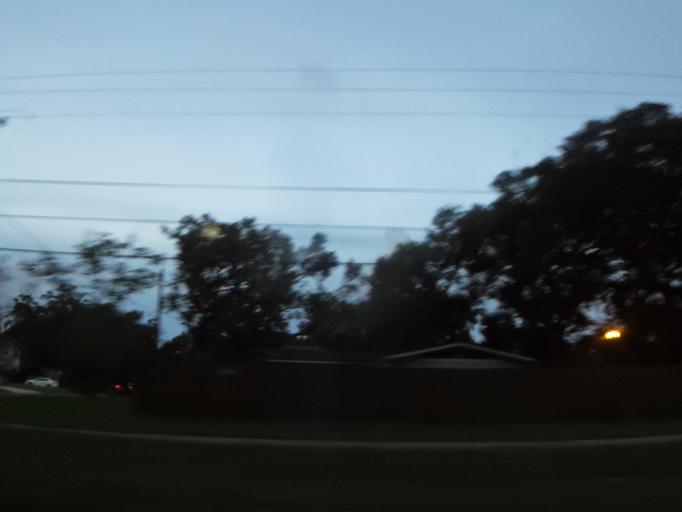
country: US
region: Florida
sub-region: Duval County
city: Jacksonville
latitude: 30.3733
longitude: -81.6076
